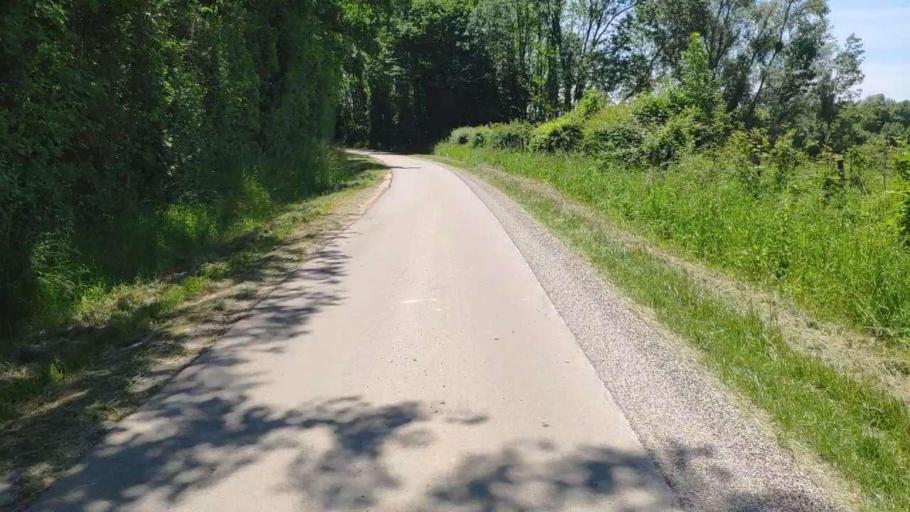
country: FR
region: Franche-Comte
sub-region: Departement du Jura
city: Bletterans
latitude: 46.7536
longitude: 5.4032
